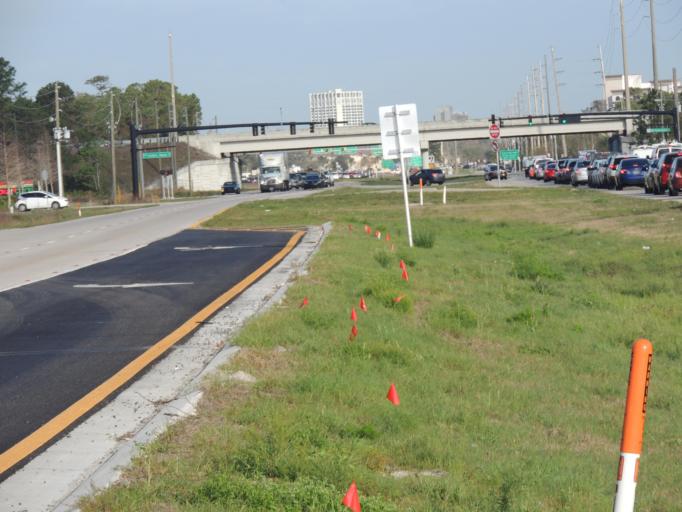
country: US
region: Florida
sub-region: Osceola County
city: Celebration
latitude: 28.3466
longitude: -81.4873
